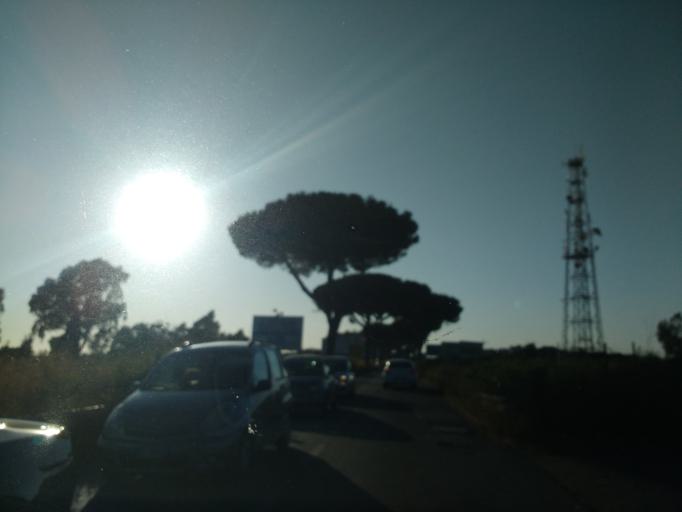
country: IT
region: Latium
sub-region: Citta metropolitana di Roma Capitale
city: Vitinia
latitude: 41.7658
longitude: 12.3818
